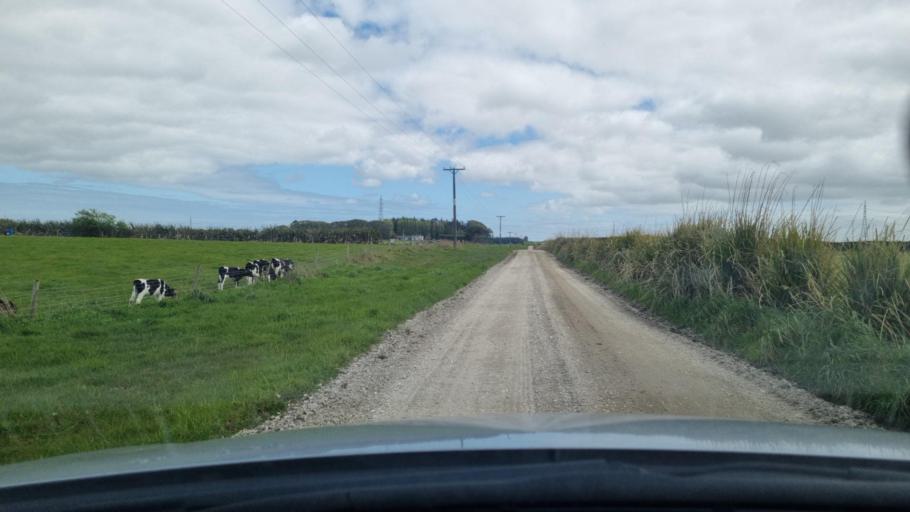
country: NZ
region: Southland
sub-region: Invercargill City
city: Invercargill
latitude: -46.4558
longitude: 168.4574
